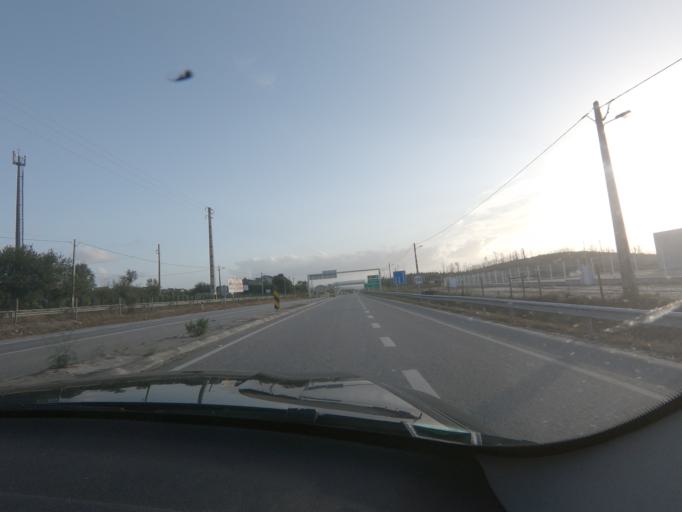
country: PT
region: Viseu
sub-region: Santa Comba Dao
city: Santa Comba Dao
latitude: 40.3601
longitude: -8.1366
